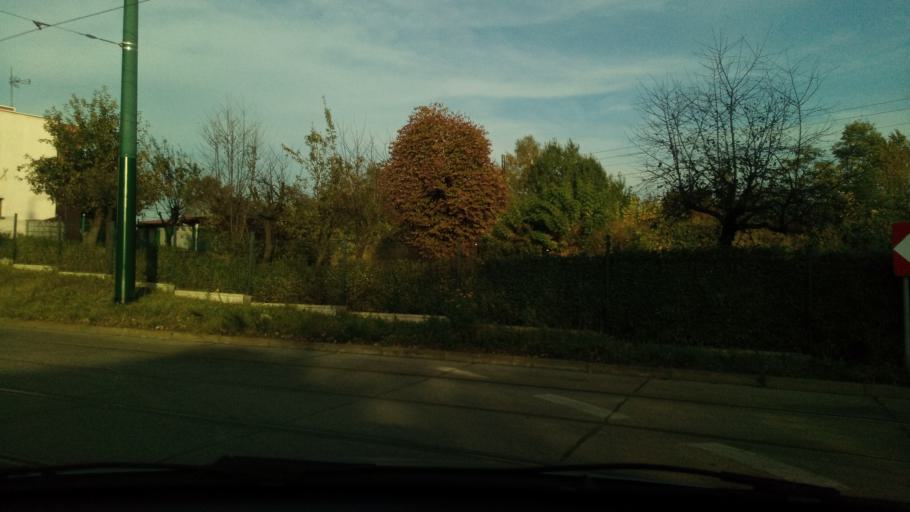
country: PL
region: Silesian Voivodeship
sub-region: Sosnowiec
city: Sosnowiec
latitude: 50.2639
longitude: 19.1073
